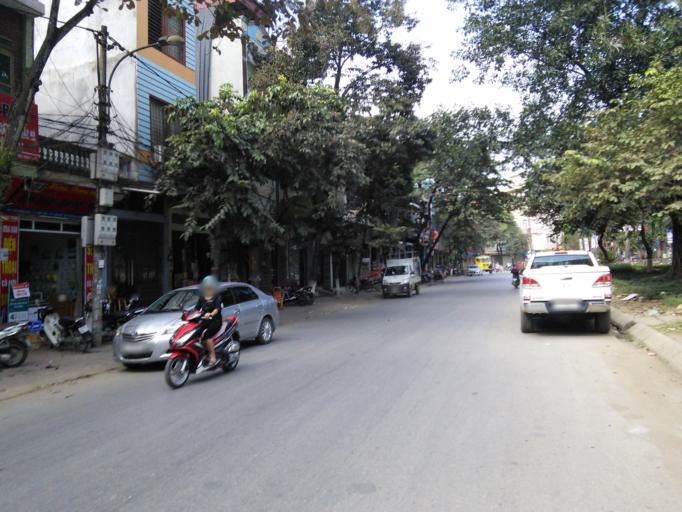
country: VN
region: Lao Cai
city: Lao Cai
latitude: 22.4741
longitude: 103.9730
